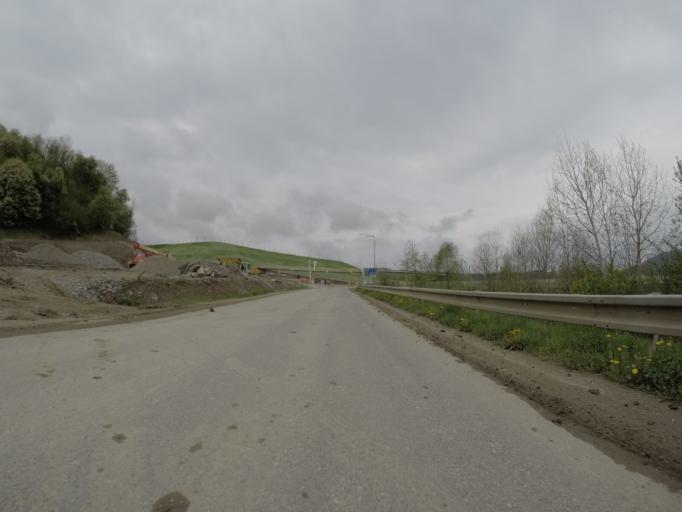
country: SK
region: Banskobystricky
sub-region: Okres Banska Bystrica
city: Brezno
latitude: 48.7983
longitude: 19.6403
